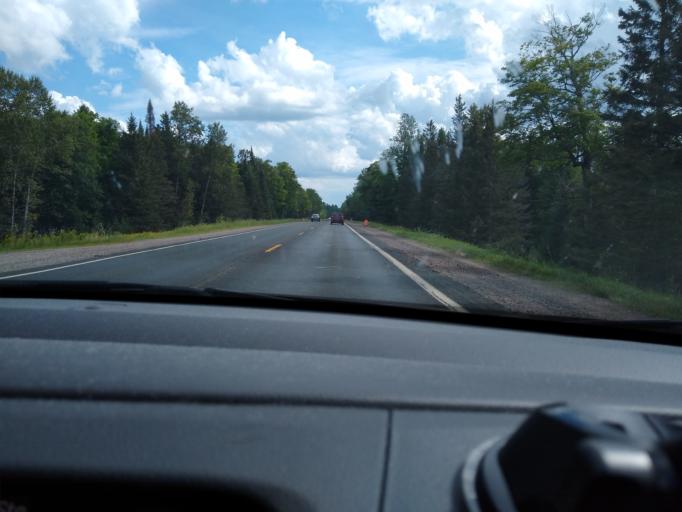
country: US
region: Michigan
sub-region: Iron County
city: Crystal Falls
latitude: 46.2666
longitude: -88.0167
